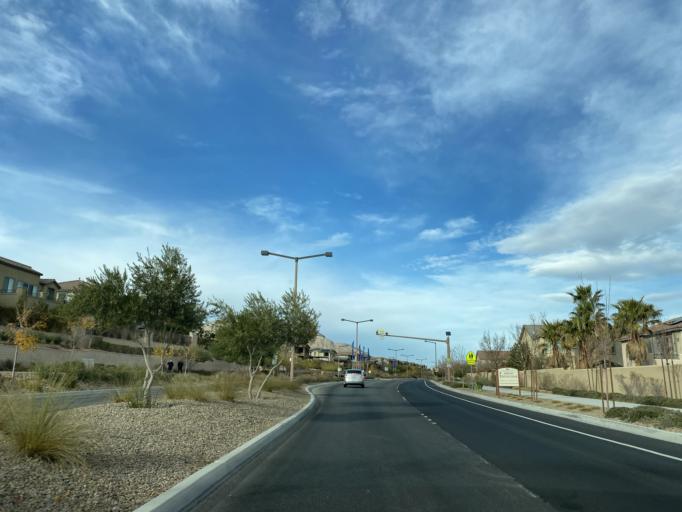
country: US
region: Nevada
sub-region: Clark County
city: Summerlin South
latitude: 36.1732
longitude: -115.3555
